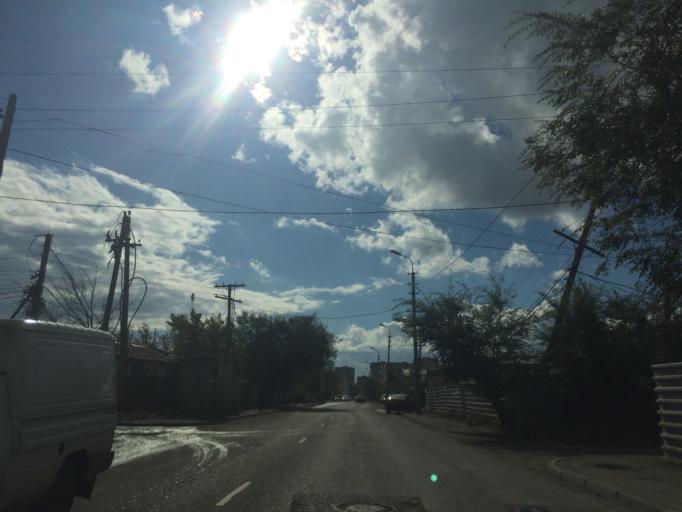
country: KZ
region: Astana Qalasy
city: Astana
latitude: 51.1875
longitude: 71.3835
